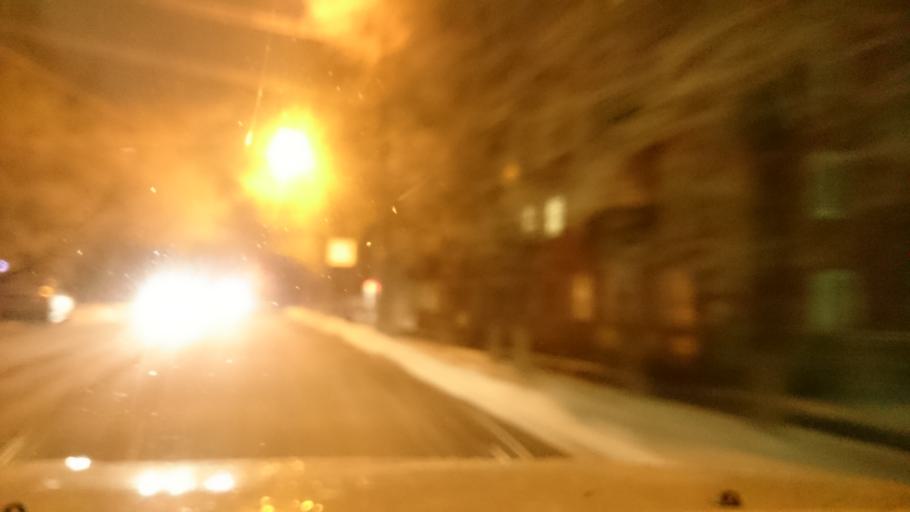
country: RU
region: Tula
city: Mendeleyevskiy
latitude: 54.1642
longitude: 37.5774
